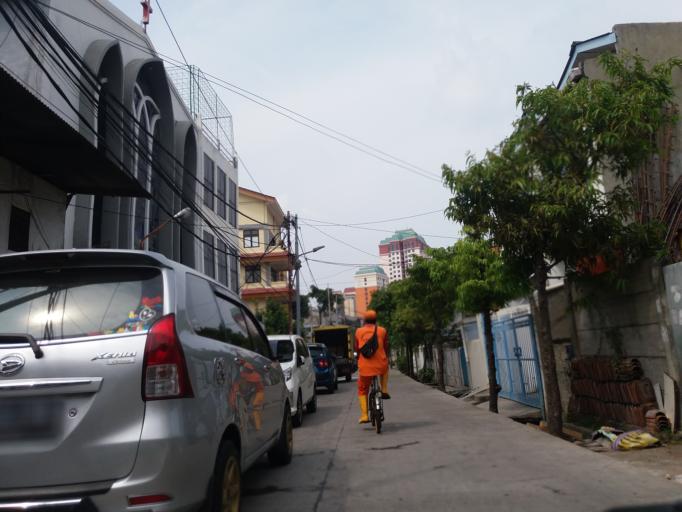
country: ID
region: Jakarta Raya
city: Jakarta
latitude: -6.1383
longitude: 106.8191
